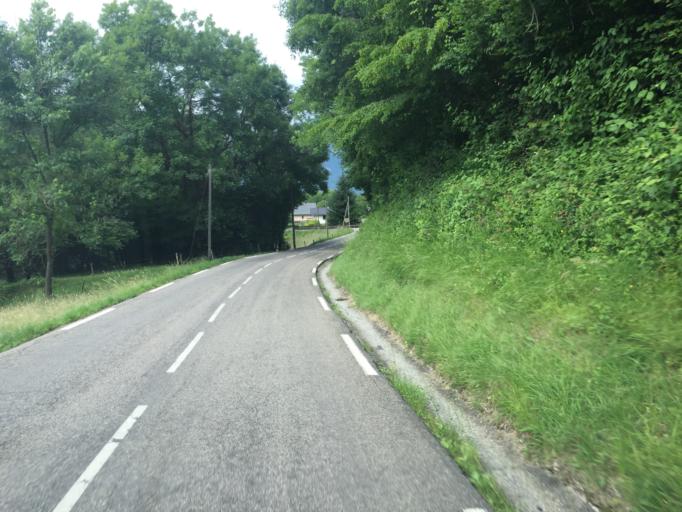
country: FR
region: Rhone-Alpes
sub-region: Departement de la Savoie
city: Jacob-Bellecombette
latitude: 45.5390
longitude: 5.9164
